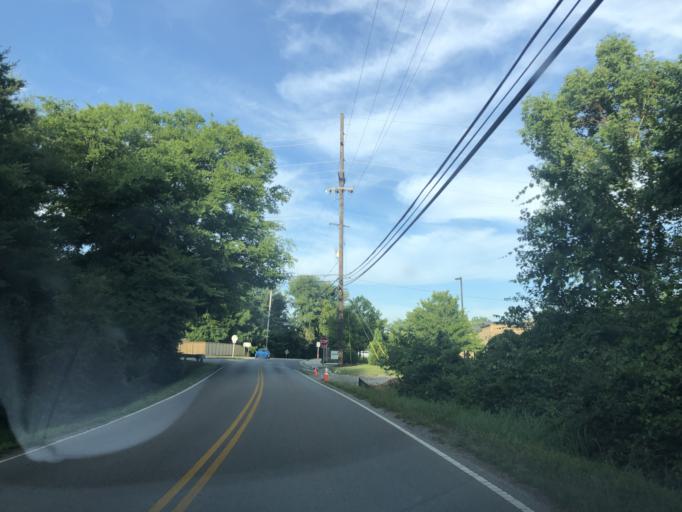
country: US
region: Tennessee
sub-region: Davidson County
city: Belle Meade
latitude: 36.0625
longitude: -86.9244
